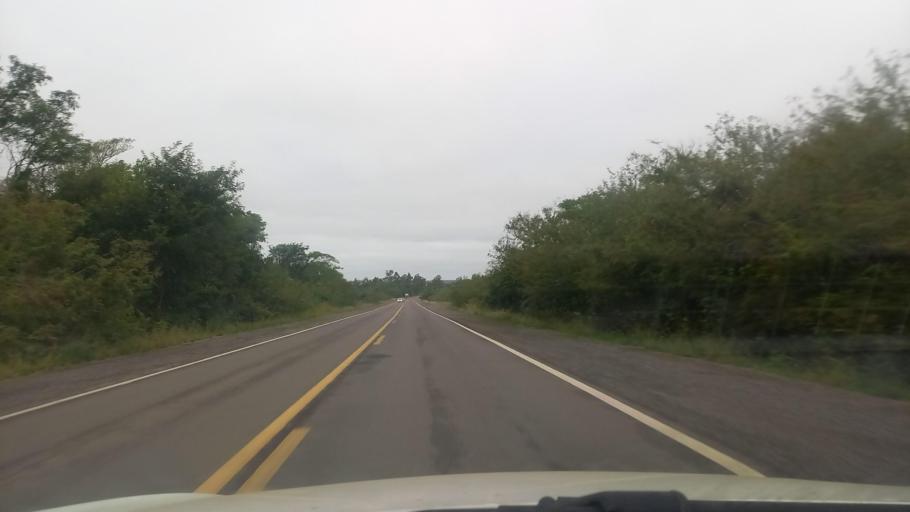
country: BR
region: Rio Grande do Sul
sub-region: Sao Pedro Do Sul
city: Sao Pedro do Sul
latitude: -29.7913
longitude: -54.1187
